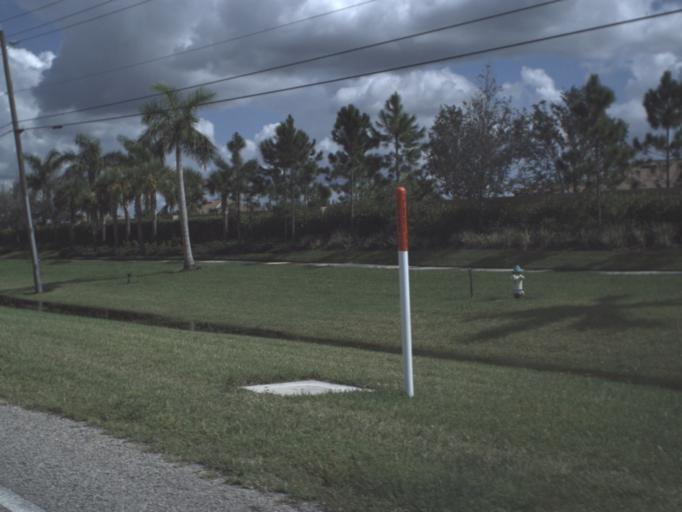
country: US
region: Florida
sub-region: Sarasota County
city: Plantation
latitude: 27.0495
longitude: -82.3496
